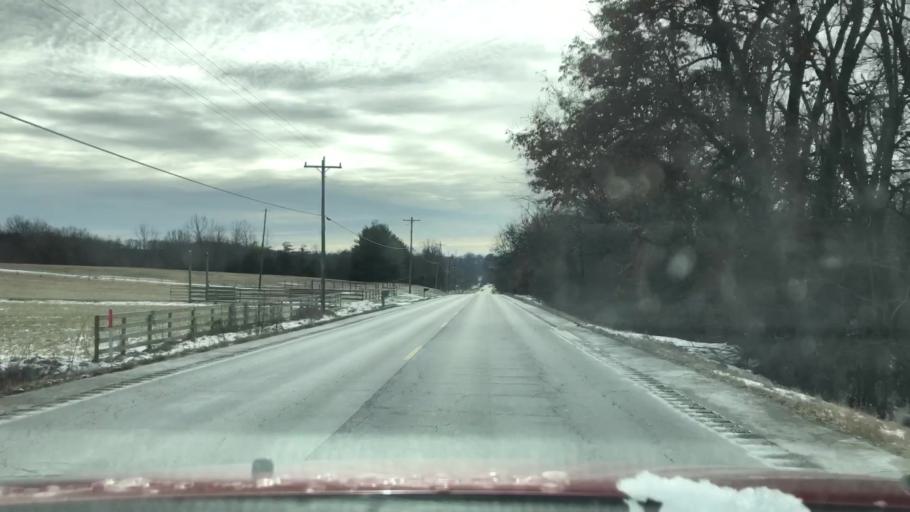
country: US
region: Missouri
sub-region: Jackson County
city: Oak Grove
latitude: 38.9506
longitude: -94.1317
